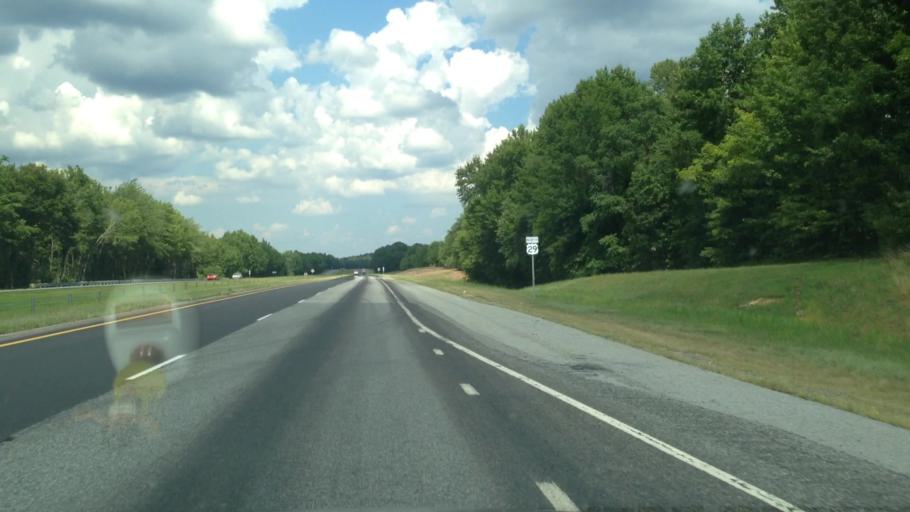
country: US
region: North Carolina
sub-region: Rockingham County
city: Reidsville
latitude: 36.4605
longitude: -79.5367
